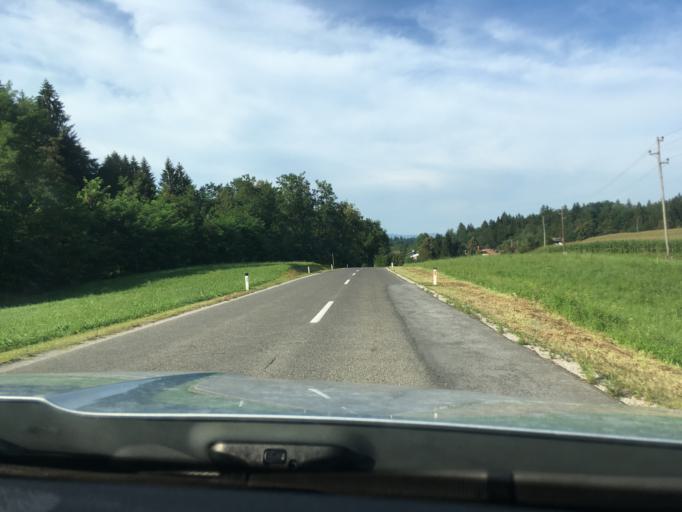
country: SI
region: Crnomelj
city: Crnomelj
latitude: 45.5944
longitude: 15.2278
